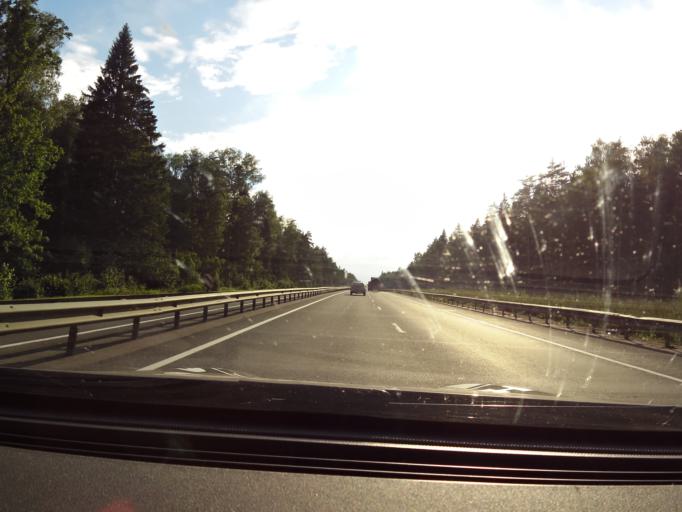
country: RU
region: Vladimir
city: Melekhovo
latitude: 56.2064
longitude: 41.1989
